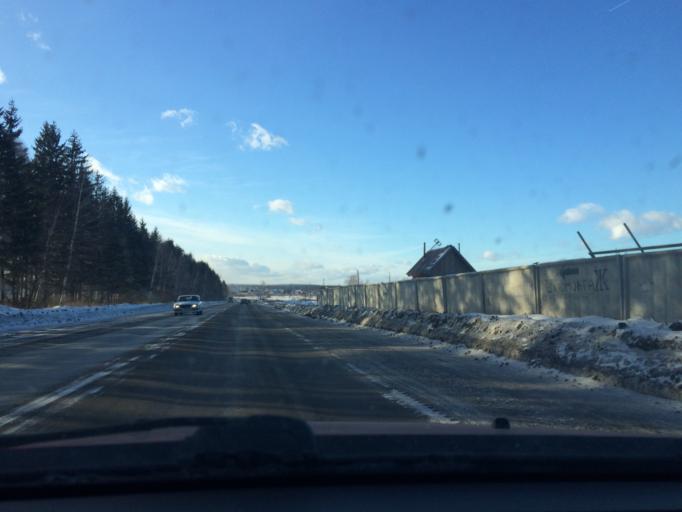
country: RU
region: Sverdlovsk
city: Aramil
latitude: 56.7719
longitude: 60.8635
